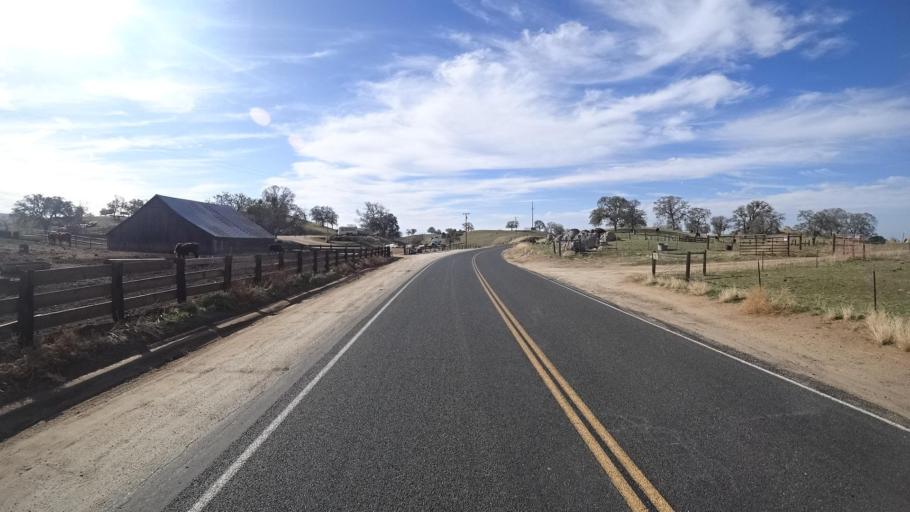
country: US
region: California
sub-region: Kern County
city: Oildale
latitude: 35.6193
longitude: -118.8495
